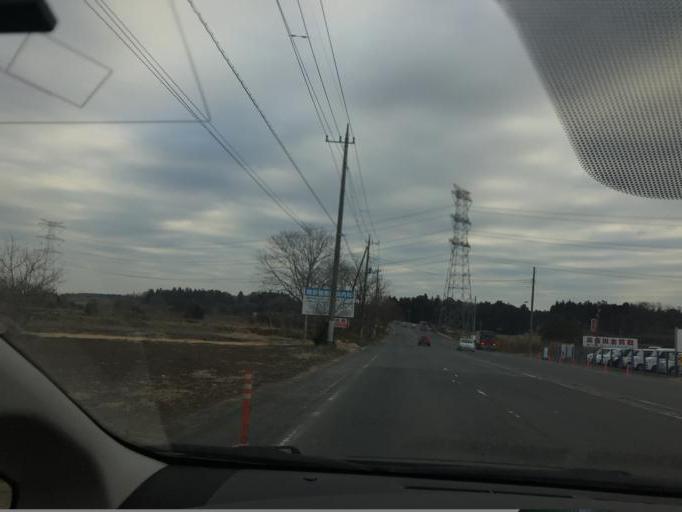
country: JP
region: Ibaraki
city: Mitsukaido
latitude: 36.0491
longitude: 140.0451
